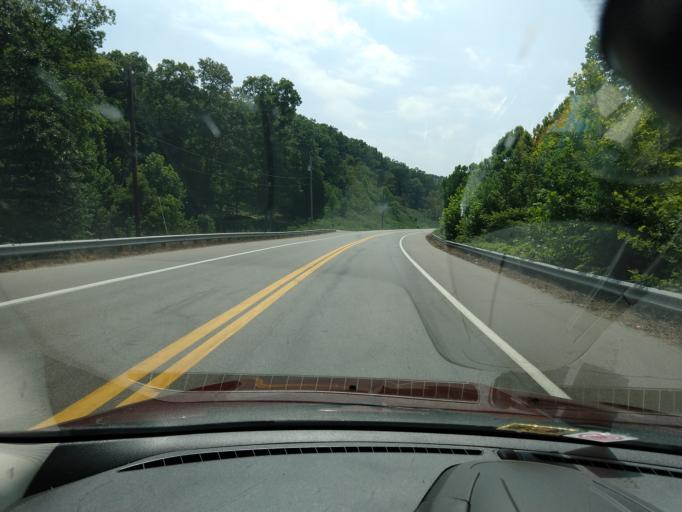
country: US
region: West Virginia
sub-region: Jackson County
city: Ravenswood
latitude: 38.8594
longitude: -81.8062
